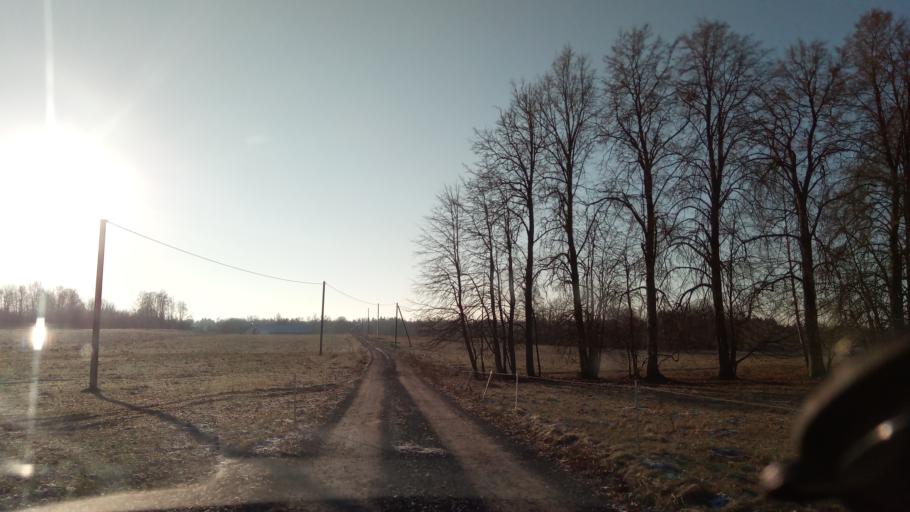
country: LT
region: Alytaus apskritis
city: Druskininkai
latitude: 54.1403
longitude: 23.9832
